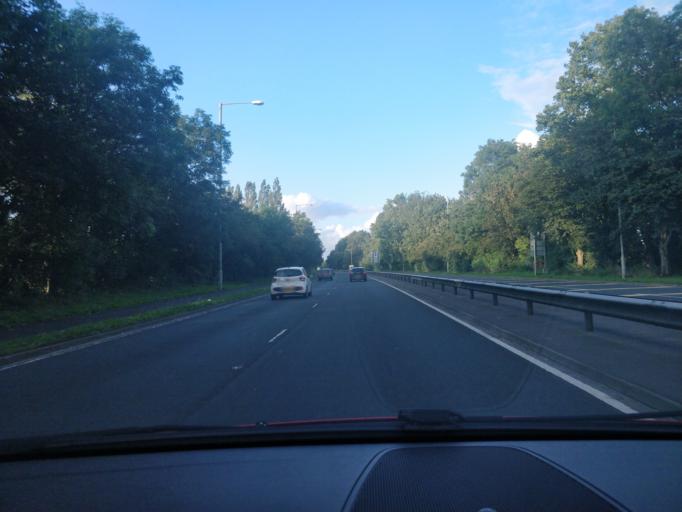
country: GB
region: England
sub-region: Lancashire
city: Croston
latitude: 53.7144
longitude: -2.7756
